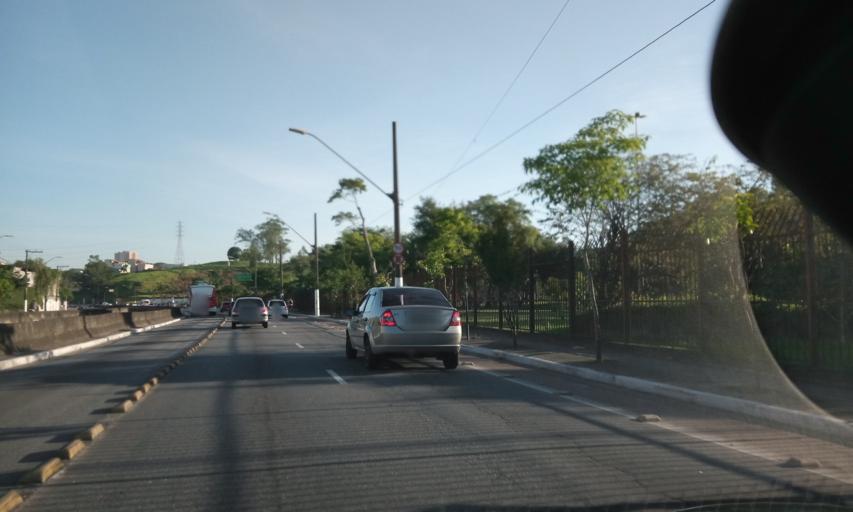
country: BR
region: Sao Paulo
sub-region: Santo Andre
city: Santo Andre
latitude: -23.6833
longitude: -46.5057
